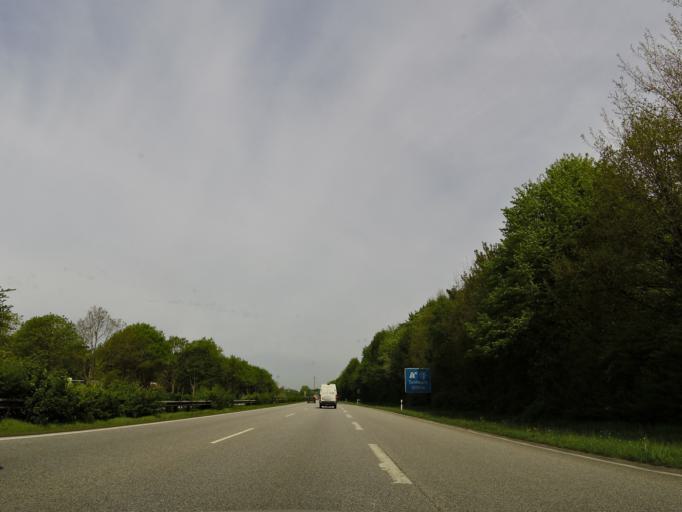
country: DE
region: Schleswig-Holstein
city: Kummerfeld
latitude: 53.7054
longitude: 9.7716
